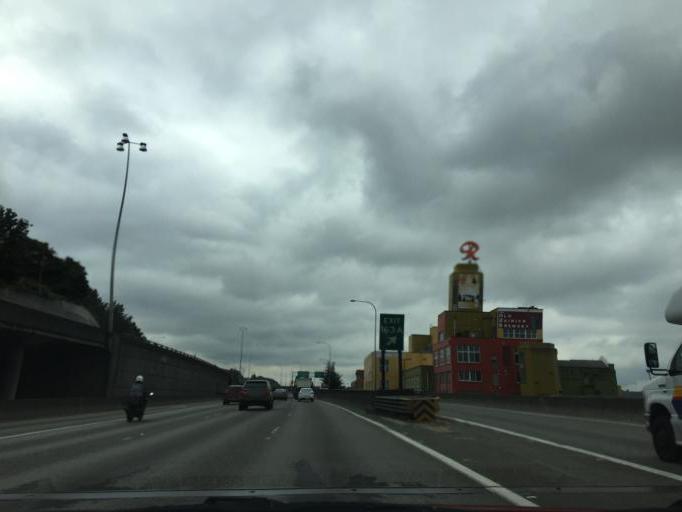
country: US
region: Washington
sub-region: King County
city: Seattle
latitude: 47.5767
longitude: -122.3199
